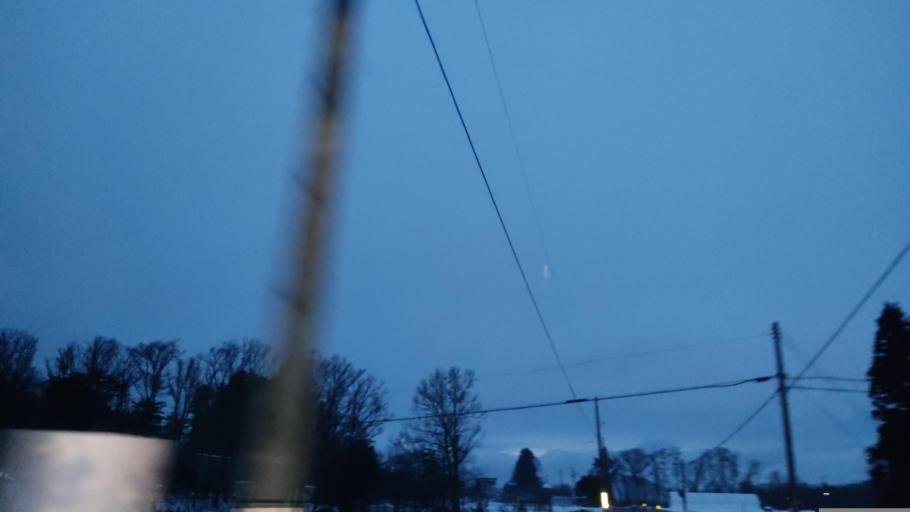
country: JP
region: Iwate
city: Morioka-shi
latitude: 39.6284
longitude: 141.1075
